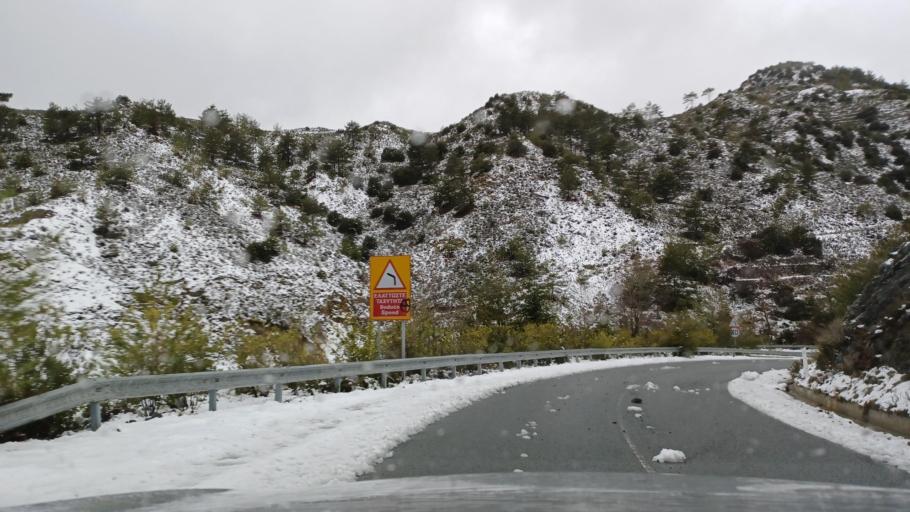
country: CY
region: Limassol
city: Pelendri
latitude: 34.8985
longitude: 32.9616
